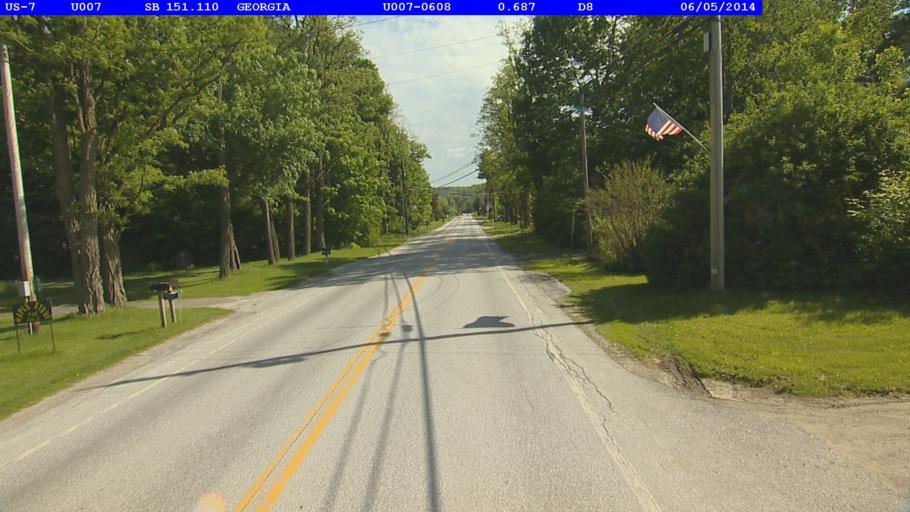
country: US
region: Vermont
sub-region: Chittenden County
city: Milton
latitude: 44.6889
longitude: -73.1096
